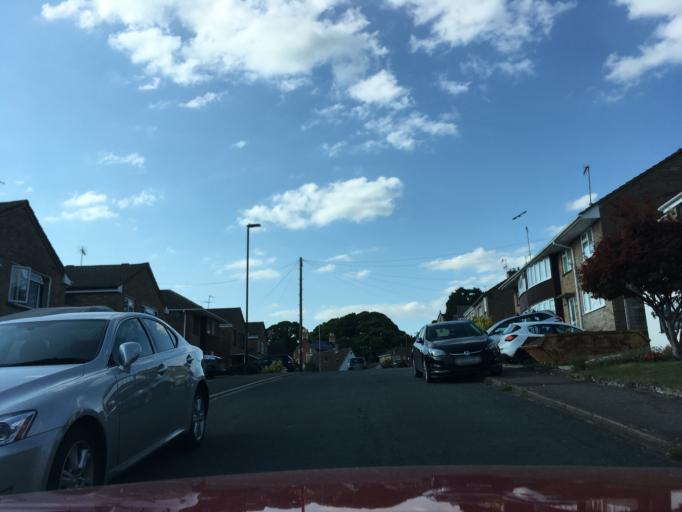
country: GB
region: England
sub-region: Gloucestershire
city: Stroud
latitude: 51.7367
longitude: -2.2300
